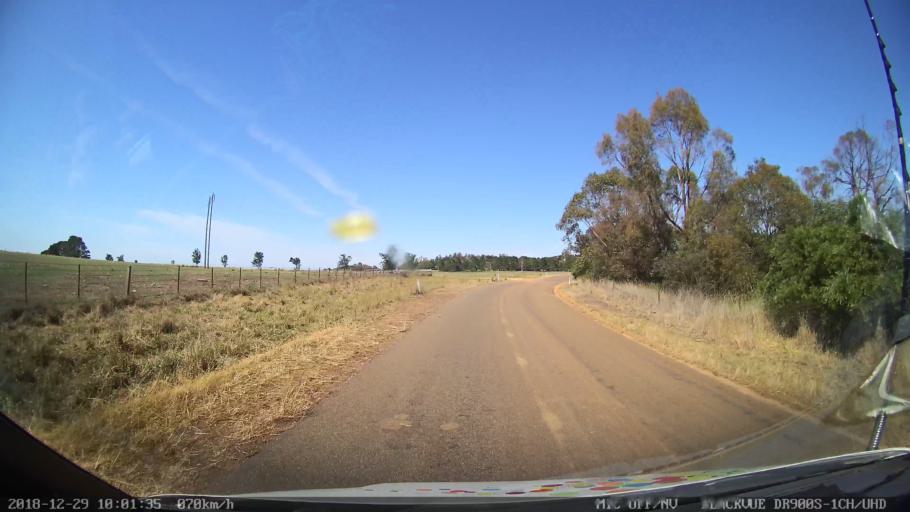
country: AU
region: New South Wales
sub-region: Goulburn Mulwaree
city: Goulburn
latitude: -34.7995
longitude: 149.4750
